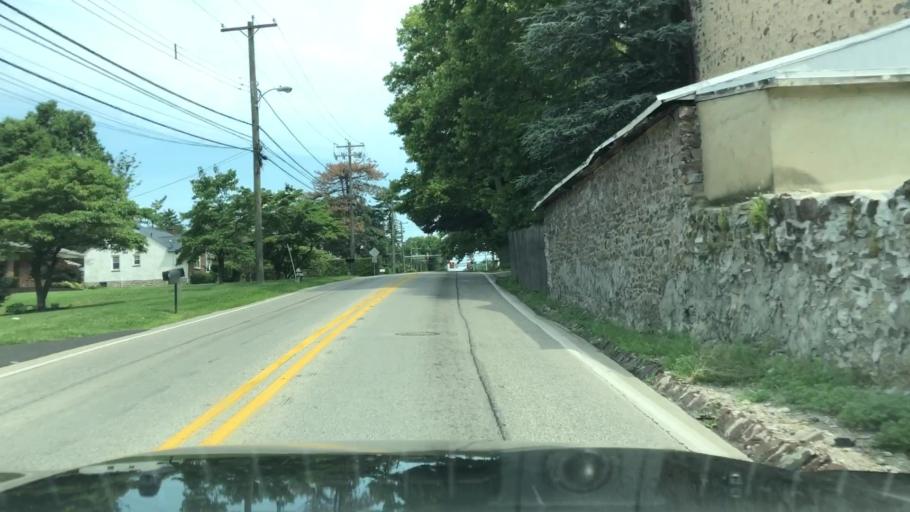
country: US
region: Pennsylvania
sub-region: Montgomery County
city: Norristown
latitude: 40.1166
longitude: -75.3072
